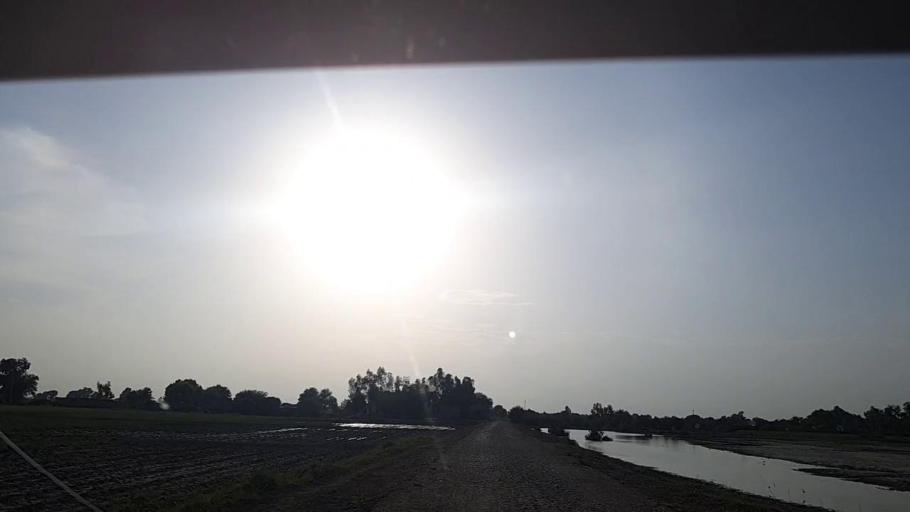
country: PK
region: Sindh
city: Khanpur
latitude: 27.8067
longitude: 69.3324
